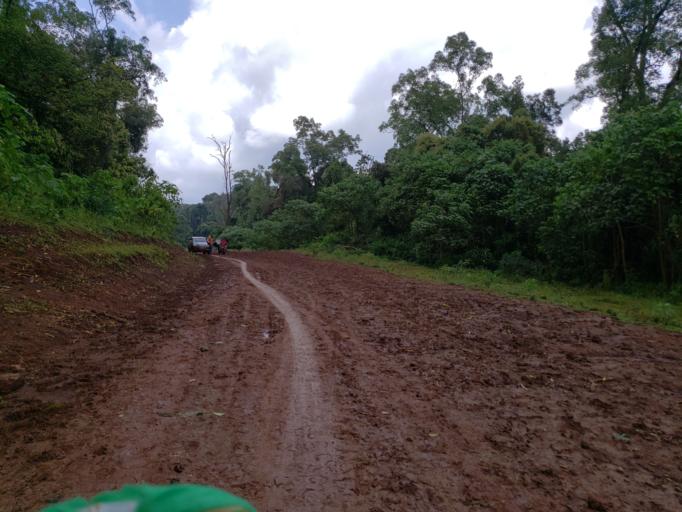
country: ET
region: Oromiya
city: Dodola
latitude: 6.4662
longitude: 39.5304
